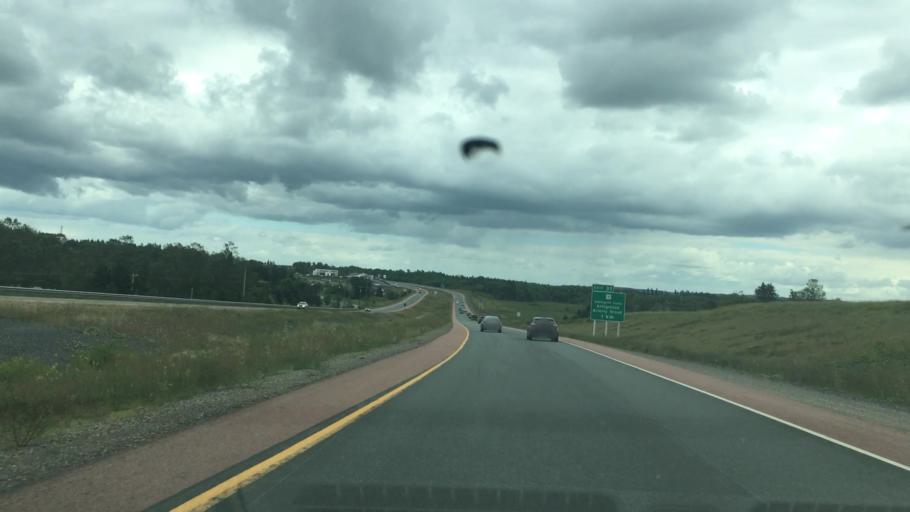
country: CA
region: Nova Scotia
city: Antigonish
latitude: 45.5968
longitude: -62.0447
